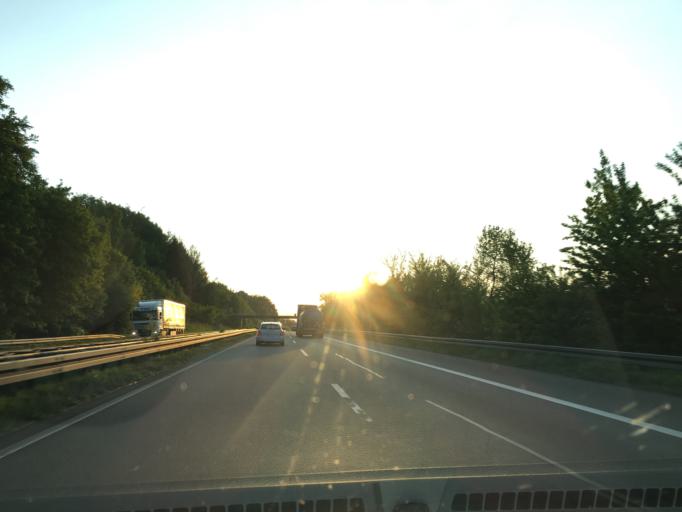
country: DE
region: Lower Saxony
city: Bissendorf
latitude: 52.2208
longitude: 8.2181
